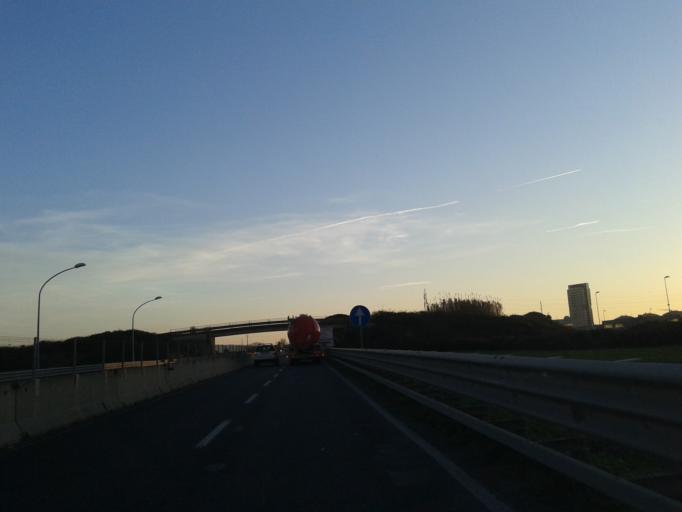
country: IT
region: Tuscany
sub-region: Provincia di Livorno
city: Livorno
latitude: 43.5678
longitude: 10.3471
